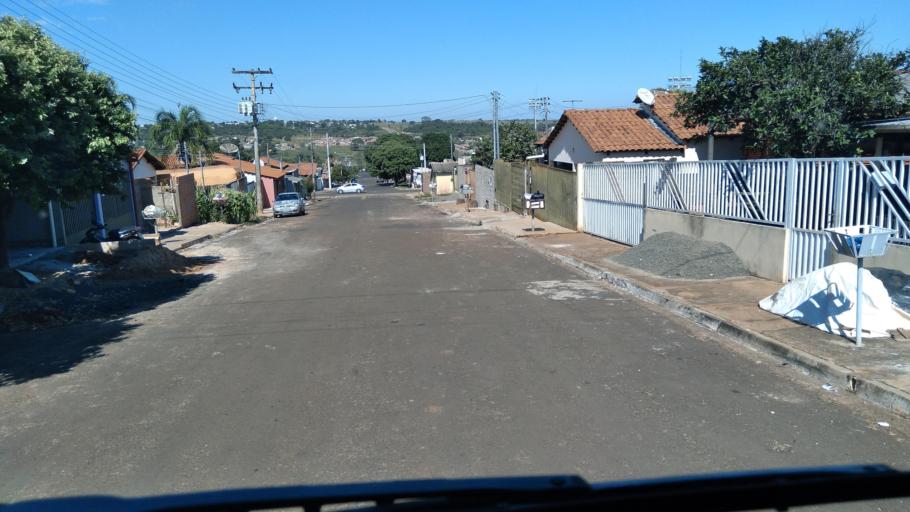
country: BR
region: Goias
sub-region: Mineiros
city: Mineiros
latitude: -17.5705
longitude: -52.5664
